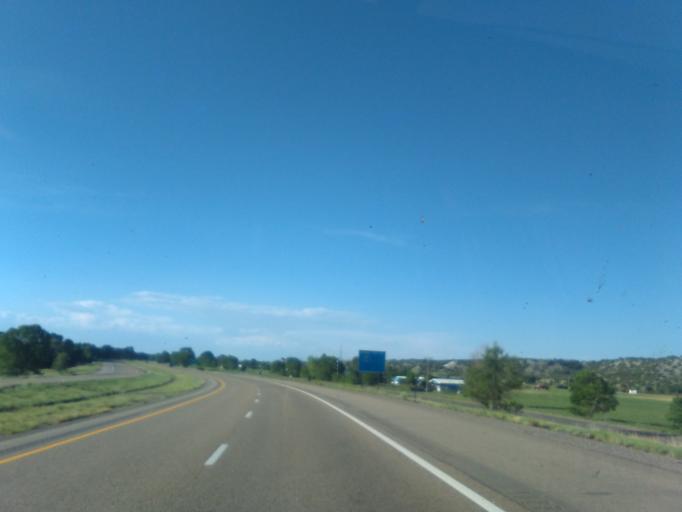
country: US
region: New Mexico
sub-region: San Miguel County
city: Las Vegas
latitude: 35.5768
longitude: -105.2117
